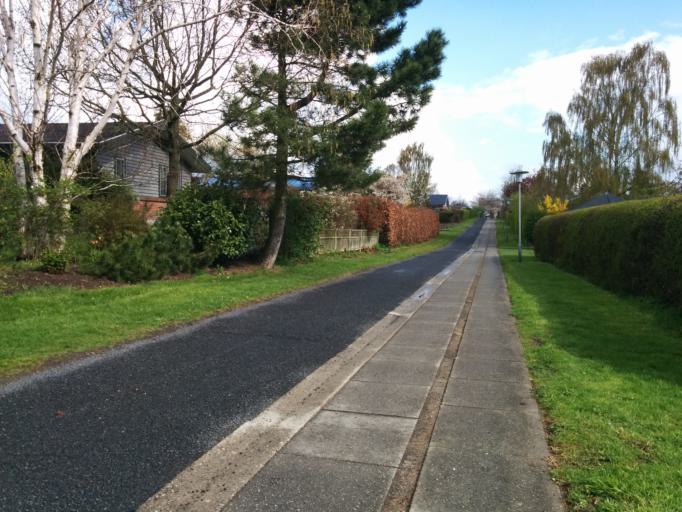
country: DK
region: Central Jutland
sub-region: Arhus Kommune
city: Hjortshoj
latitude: 56.2316
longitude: 10.3037
